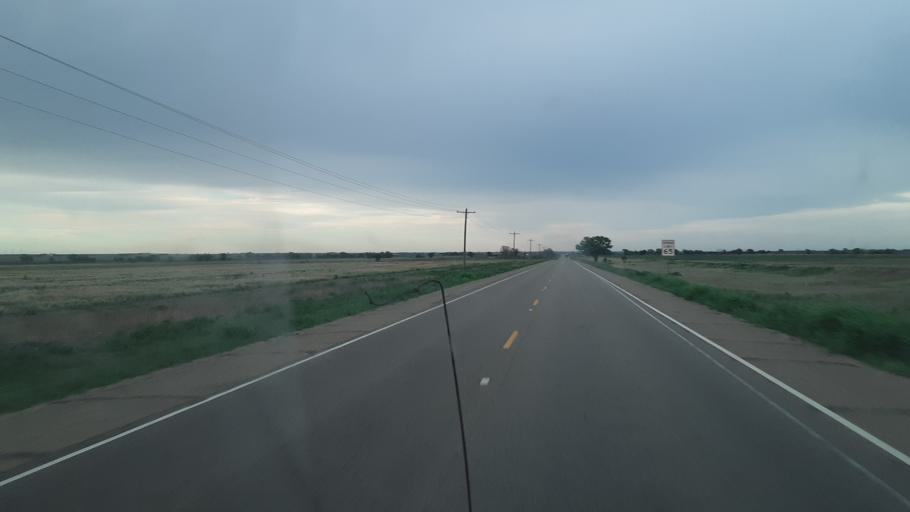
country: US
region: Colorado
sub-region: Prowers County
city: Lamar
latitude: 38.0544
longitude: -102.2463
